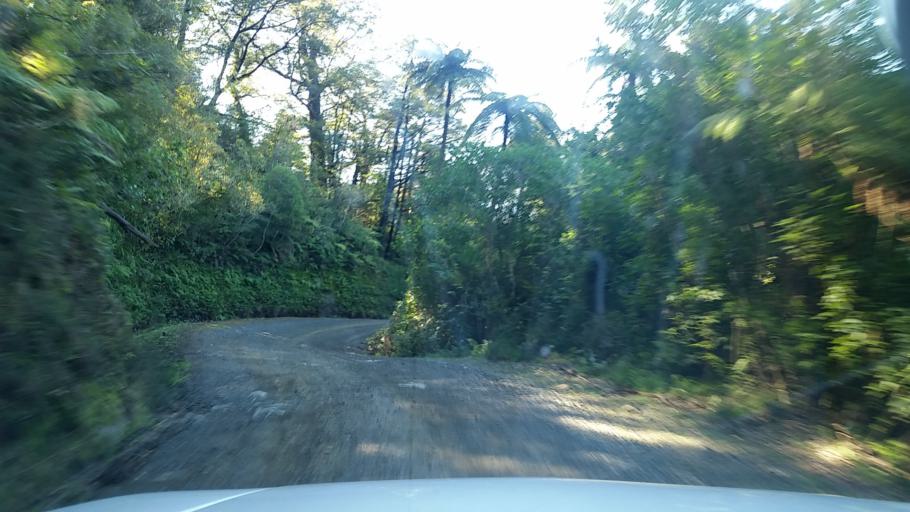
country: NZ
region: Marlborough
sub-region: Marlborough District
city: Picton
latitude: -41.1057
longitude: 173.6537
